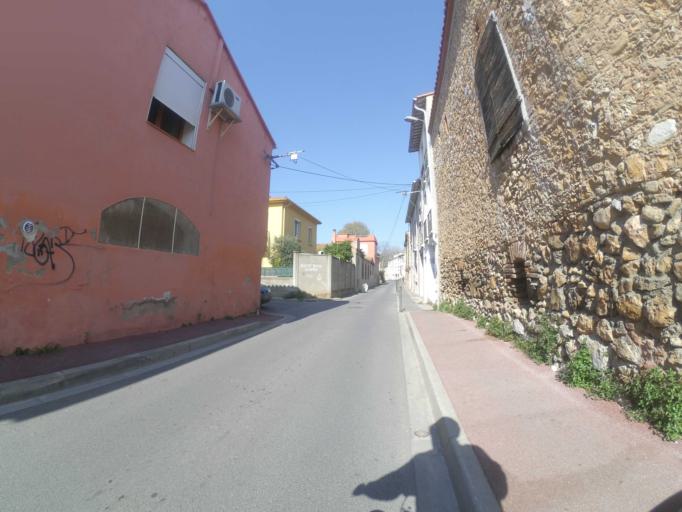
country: FR
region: Languedoc-Roussillon
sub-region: Departement des Pyrenees-Orientales
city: Thuir
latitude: 42.6317
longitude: 2.7554
